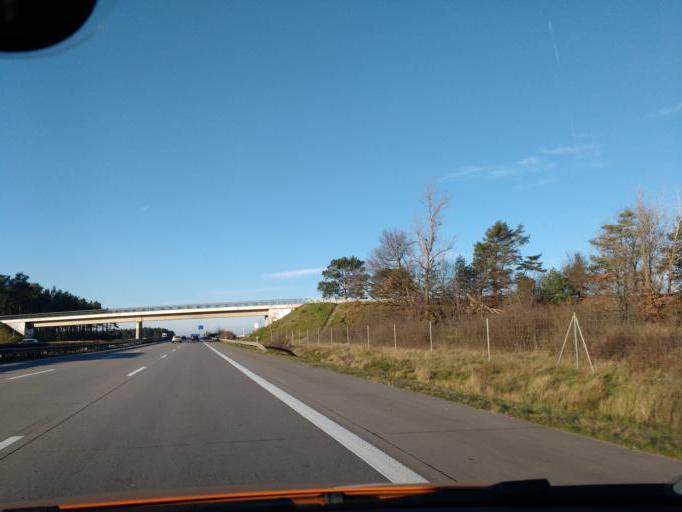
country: DE
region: Brandenburg
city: Ziesar
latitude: 52.2470
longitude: 12.2842
